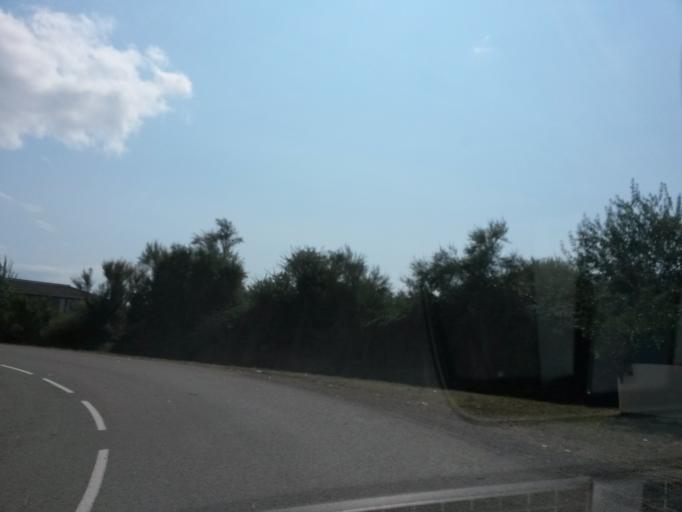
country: FR
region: Pays de la Loire
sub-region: Departement de la Vendee
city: Saint-Hilaire-de-Talmont
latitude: 46.4373
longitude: -1.6039
